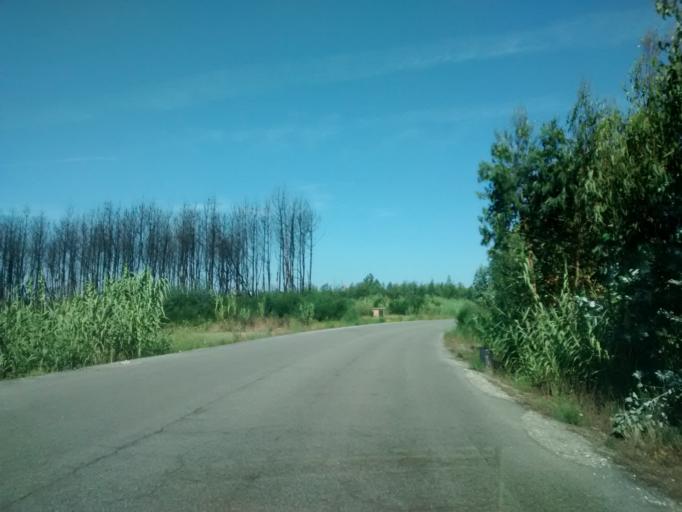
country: PT
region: Coimbra
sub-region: Mira
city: Mira
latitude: 40.4293
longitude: -8.7001
